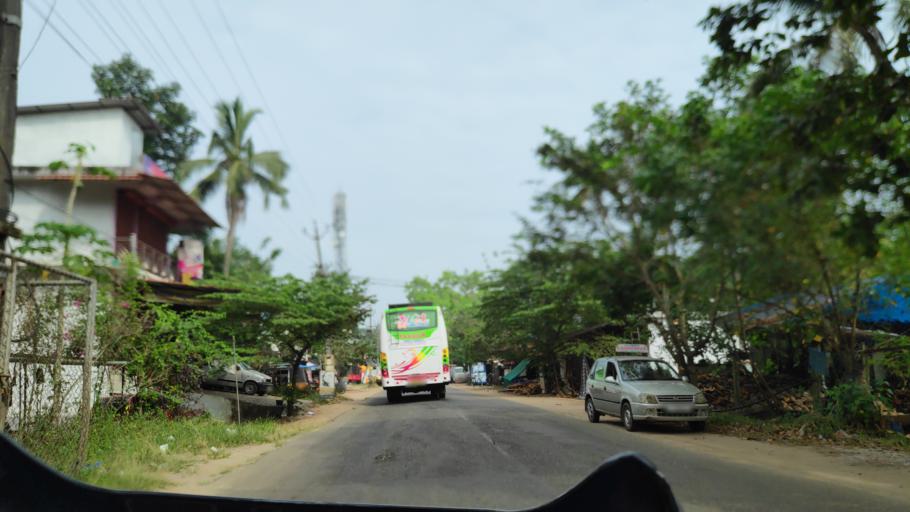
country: IN
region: Kerala
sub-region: Alappuzha
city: Kutiatodu
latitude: 9.8153
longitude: 76.3515
